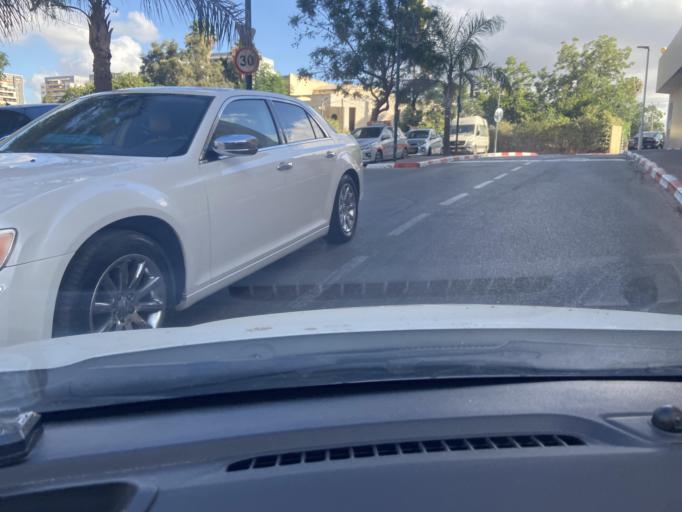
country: IL
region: Central District
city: Yehud
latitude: 32.0301
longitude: 34.8897
